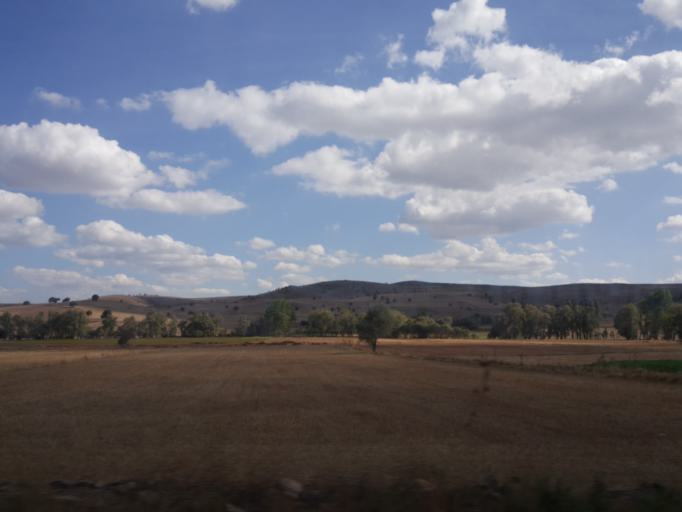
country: TR
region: Tokat
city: Camlibel
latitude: 40.1720
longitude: 36.4371
